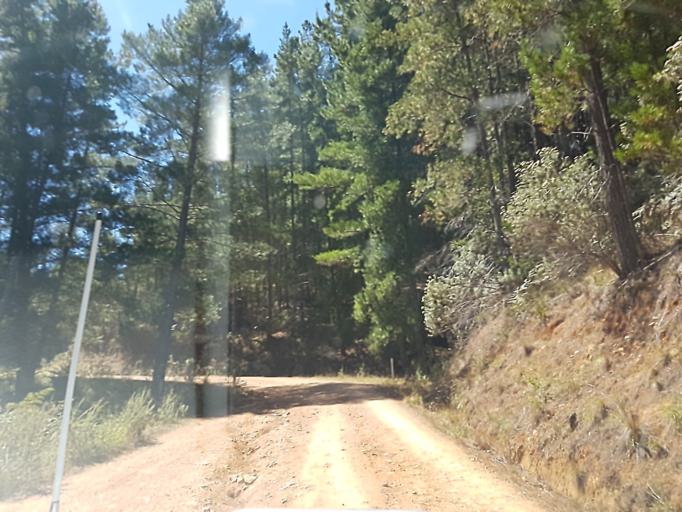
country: AU
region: Victoria
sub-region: Alpine
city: Mount Beauty
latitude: -36.7516
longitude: 146.9587
